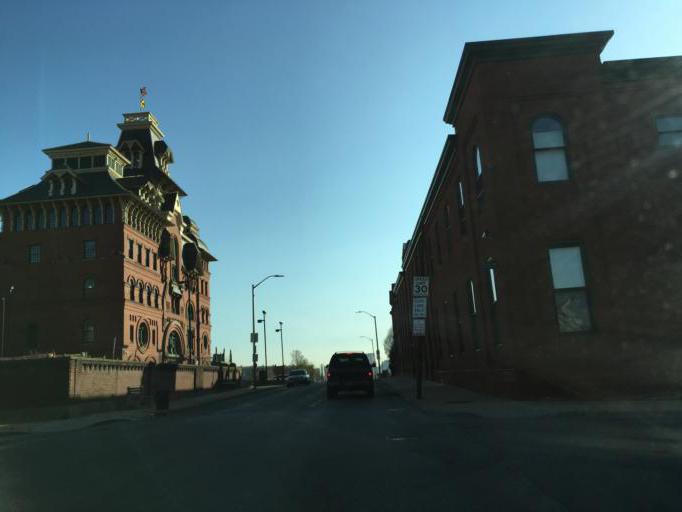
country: US
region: Maryland
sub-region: City of Baltimore
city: Baltimore
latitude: 39.3102
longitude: -76.5869
